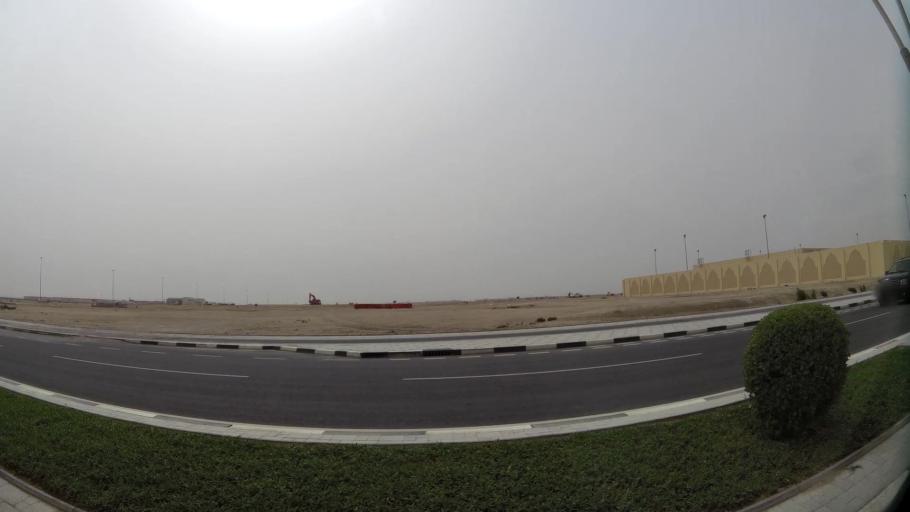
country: QA
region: Baladiyat ad Dawhah
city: Doha
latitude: 25.2237
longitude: 51.5365
